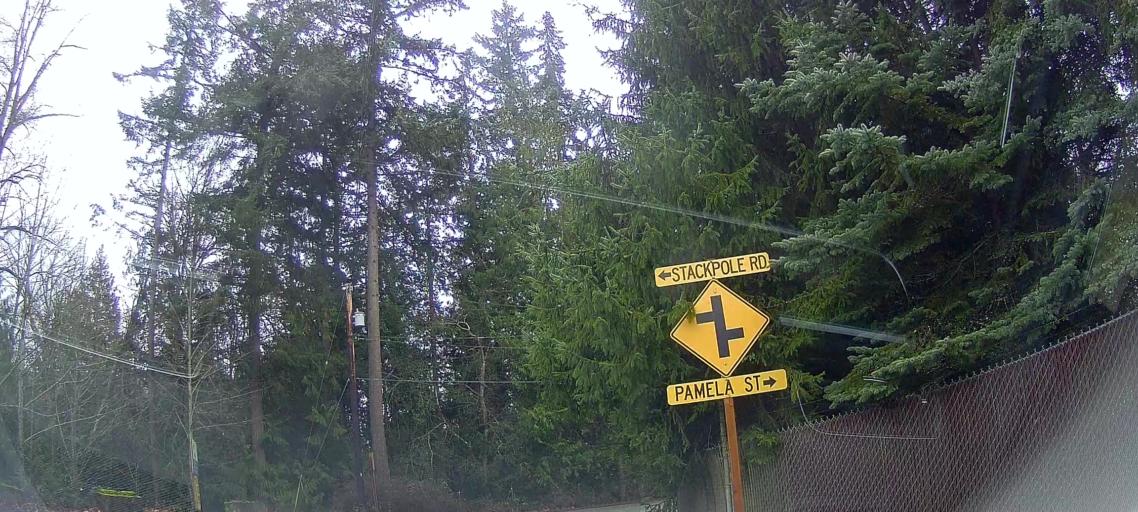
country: US
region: Washington
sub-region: Skagit County
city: Mount Vernon
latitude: 48.3848
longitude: -122.3050
